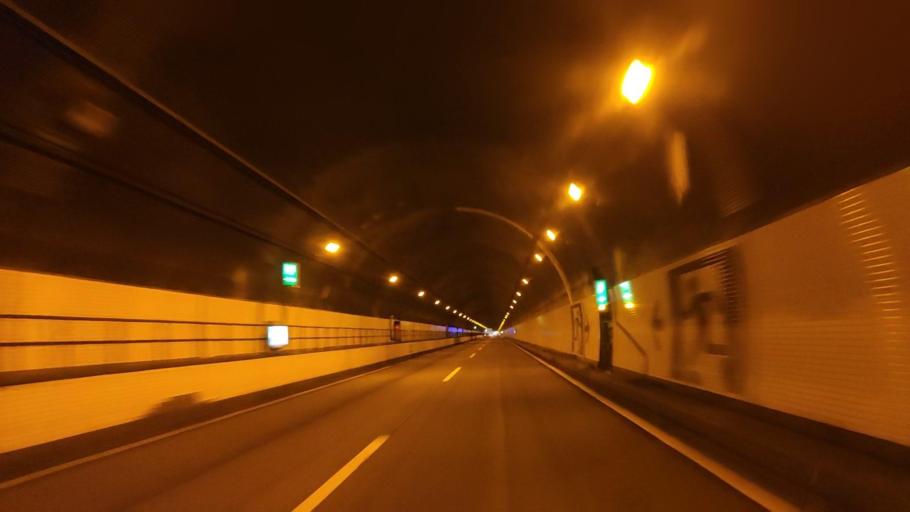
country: JP
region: Niigata
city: Itoigawa
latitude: 37.0980
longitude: 138.0083
